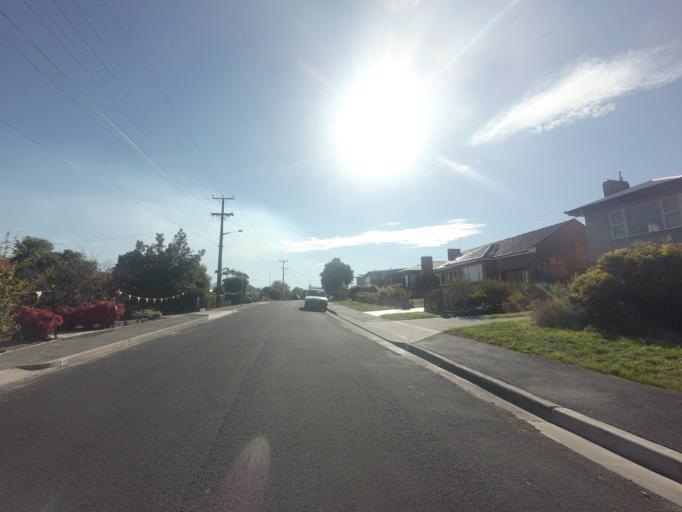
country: AU
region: Tasmania
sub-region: Clarence
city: Bellerive
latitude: -42.8732
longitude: 147.3541
